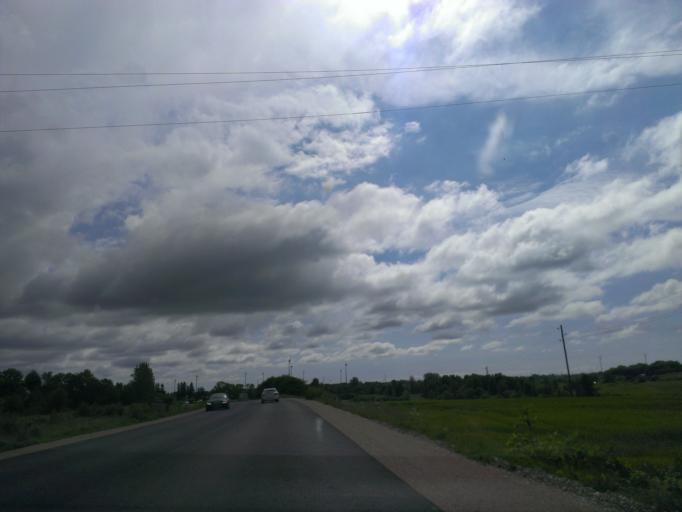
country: LV
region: Durbe
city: Liegi
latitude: 56.5595
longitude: 21.2624
